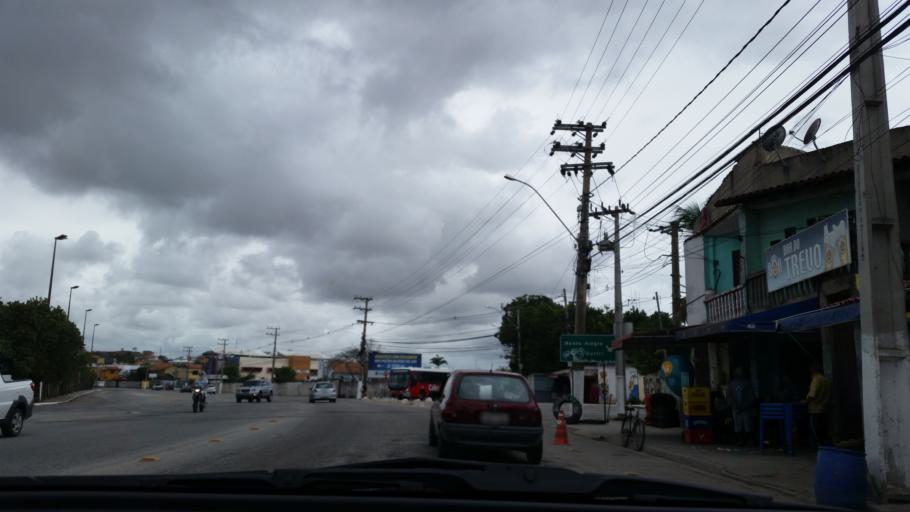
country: BR
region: Rio de Janeiro
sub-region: Cabo Frio
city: Cabo Frio
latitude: -22.8636
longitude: -42.0329
